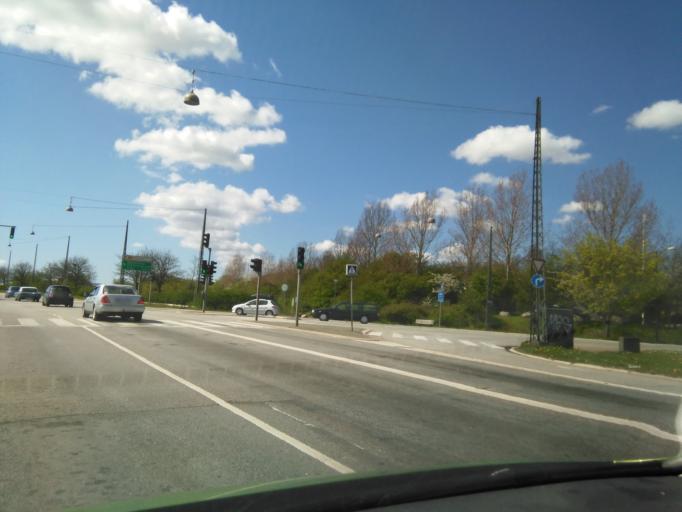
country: DK
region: Capital Region
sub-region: Kobenhavn
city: Copenhagen
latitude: 55.6416
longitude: 12.5640
